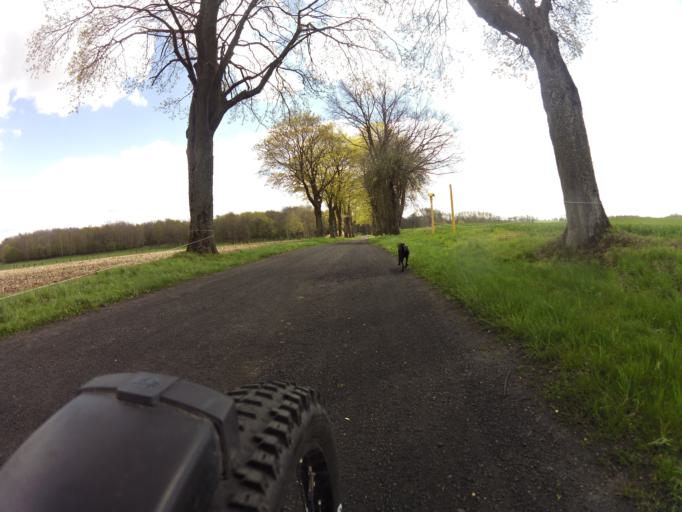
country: PL
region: West Pomeranian Voivodeship
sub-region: Powiat gryficki
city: Gryfice
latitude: 53.8496
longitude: 15.1715
